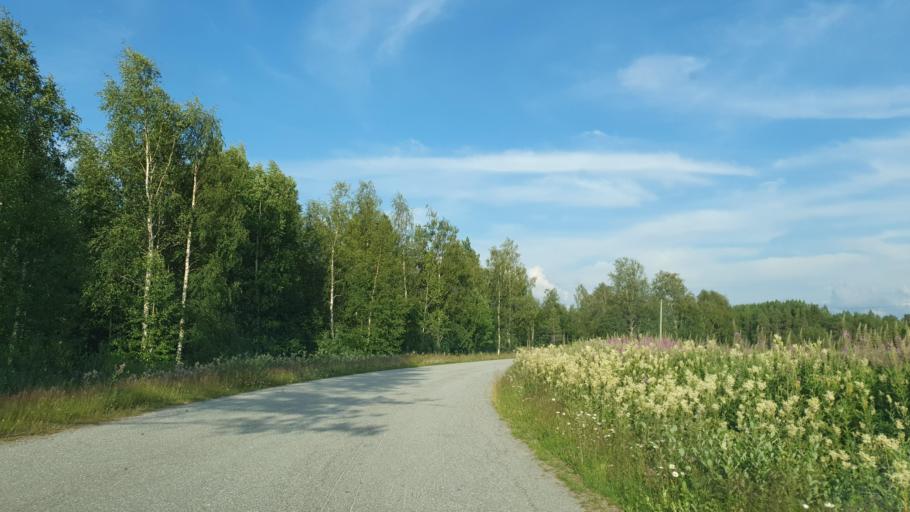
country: FI
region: Kainuu
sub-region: Kehys-Kainuu
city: Kuhmo
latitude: 64.3101
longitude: 29.5513
